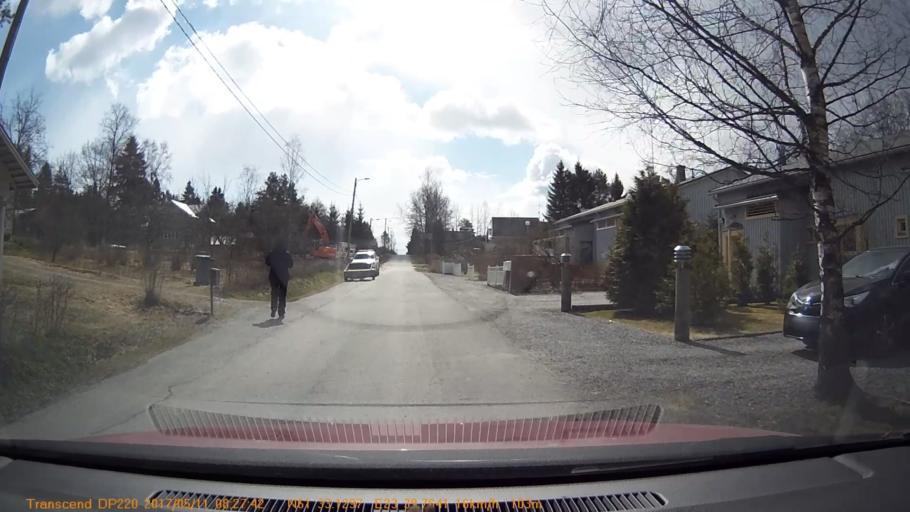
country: FI
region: Pirkanmaa
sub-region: Tampere
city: Yloejaervi
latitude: 61.5522
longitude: 23.6626
